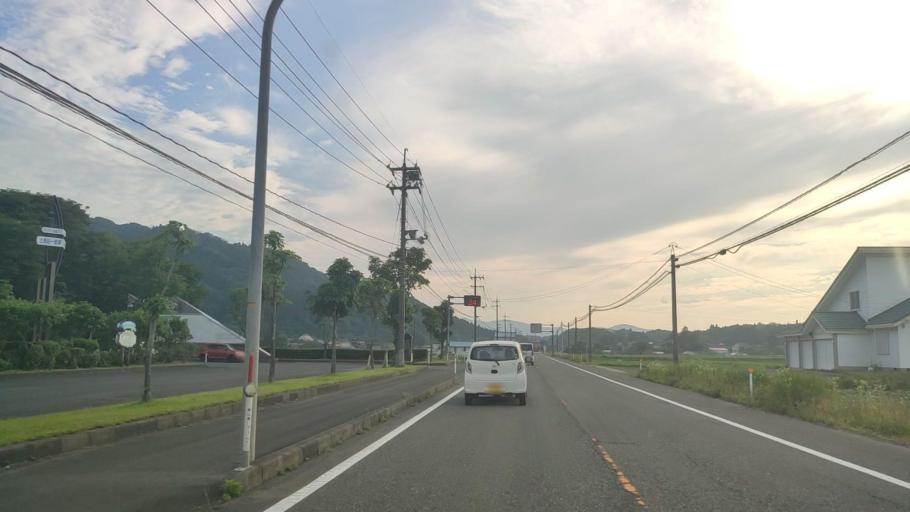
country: JP
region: Tottori
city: Kurayoshi
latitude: 35.2900
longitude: 133.7170
